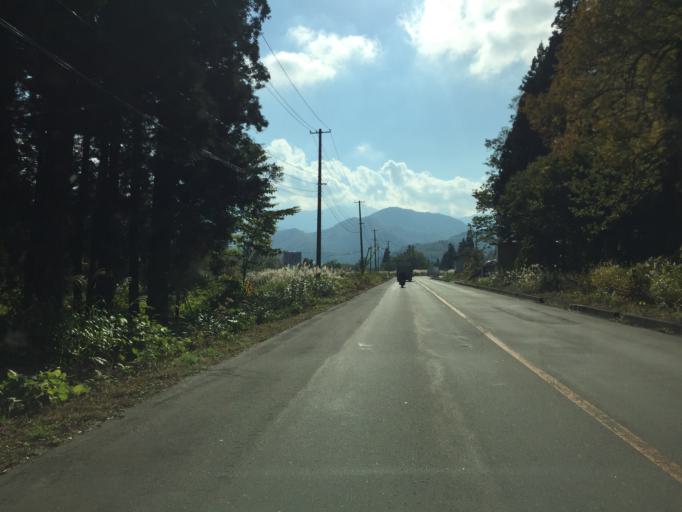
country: JP
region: Yamagata
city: Yonezawa
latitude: 37.8888
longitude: 139.9956
